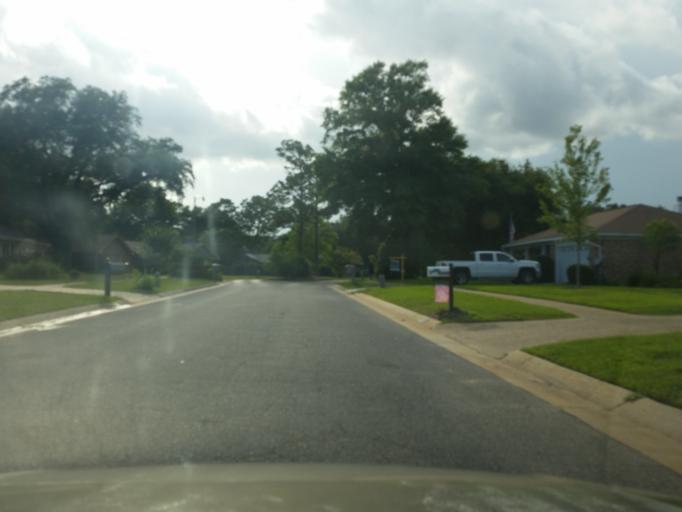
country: US
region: Florida
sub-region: Escambia County
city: Ferry Pass
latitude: 30.5005
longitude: -87.1644
